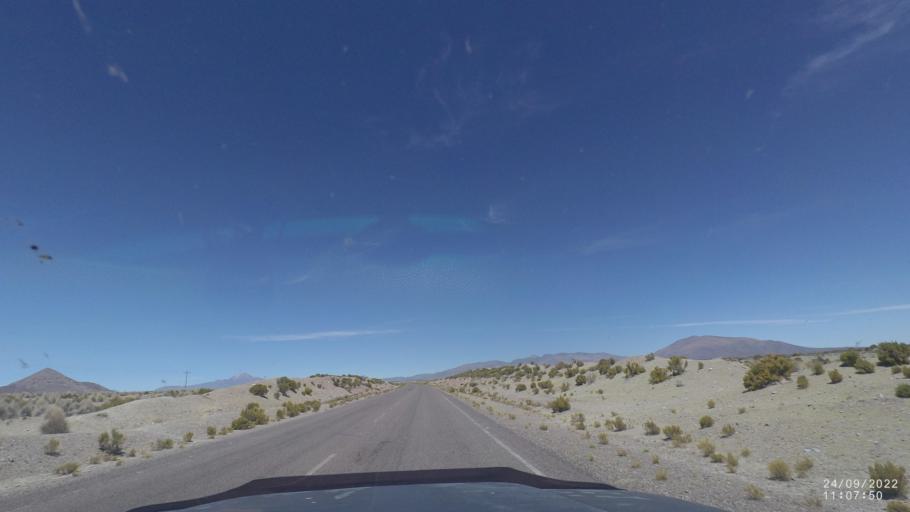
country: BO
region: Oruro
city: Challapata
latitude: -19.4800
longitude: -67.4356
